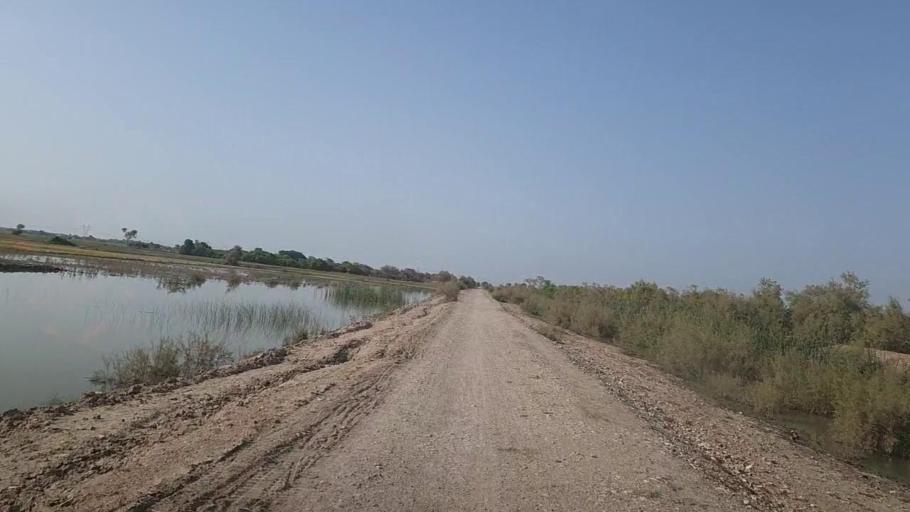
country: PK
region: Sindh
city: Sita Road
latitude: 27.0986
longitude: 67.8734
